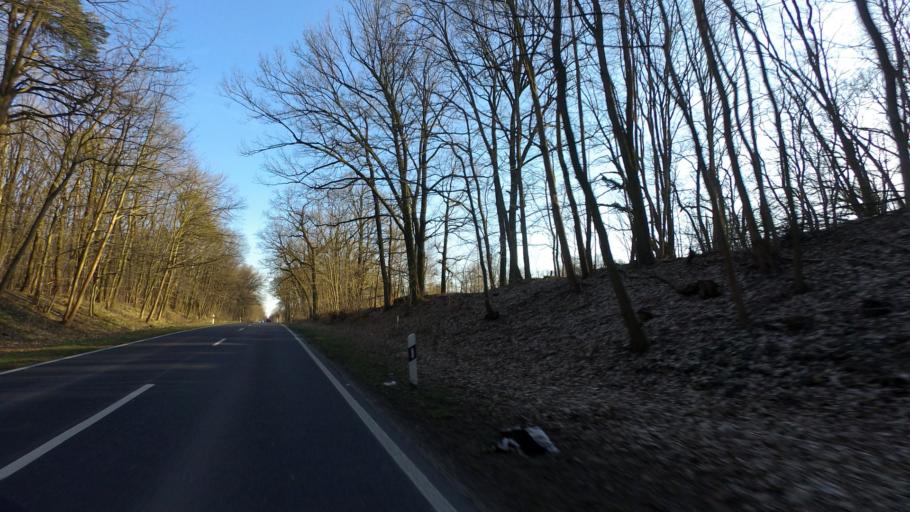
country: DE
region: Brandenburg
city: Eberswalde
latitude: 52.8242
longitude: 13.8312
